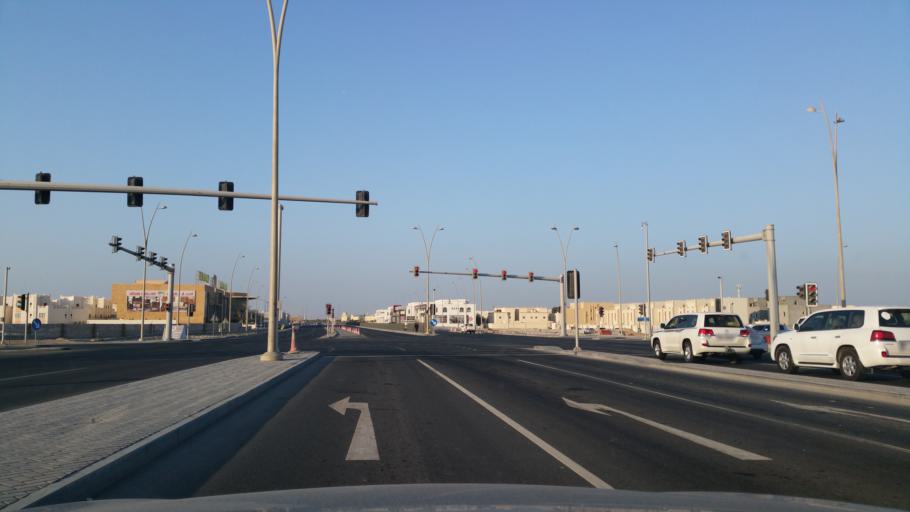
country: QA
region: Al Khawr
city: Al Khawr
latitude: 25.6631
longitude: 51.5008
